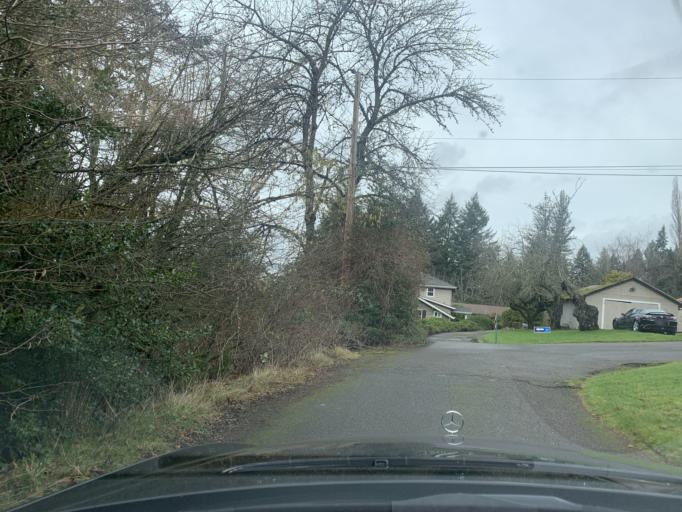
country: US
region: Oregon
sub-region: Clackamas County
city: Happy Valley
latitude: 45.4426
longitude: -122.5141
